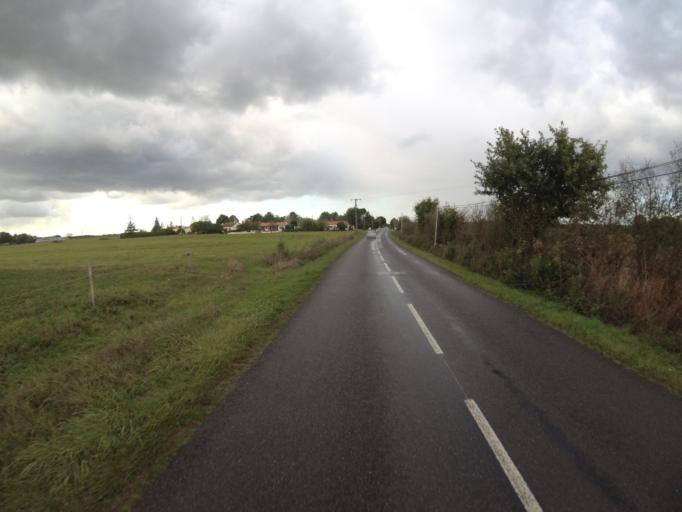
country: FR
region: Pays de la Loire
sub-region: Departement de la Loire-Atlantique
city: Saint-Hilaire-de-Clisson
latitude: 47.0695
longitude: -1.3233
